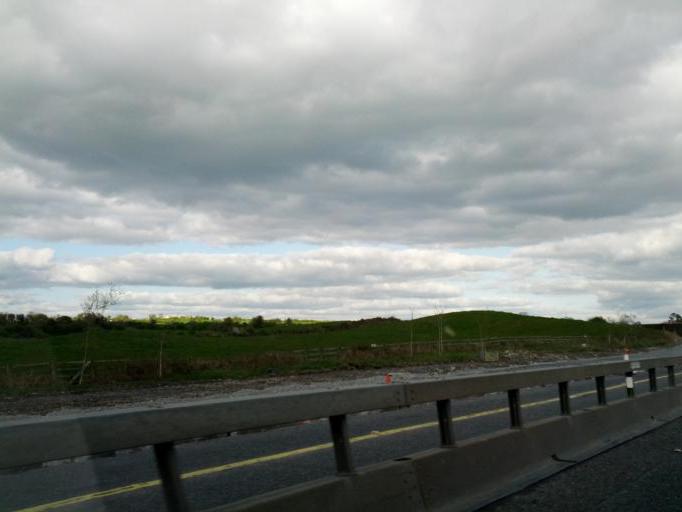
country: IE
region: Leinster
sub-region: An Iarmhi
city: Moate
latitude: 53.4003
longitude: -7.8353
